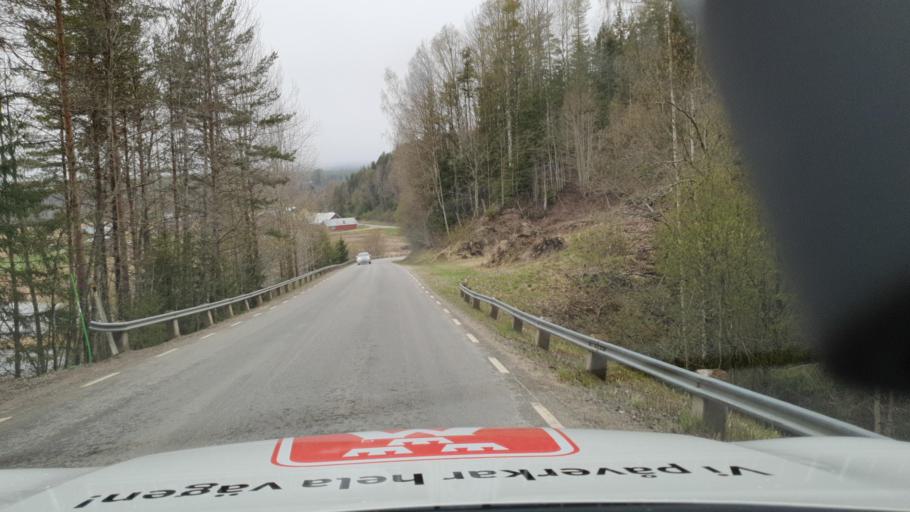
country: SE
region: Vaesterbotten
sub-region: Nordmalings Kommun
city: Nordmaling
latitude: 63.7220
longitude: 19.5348
